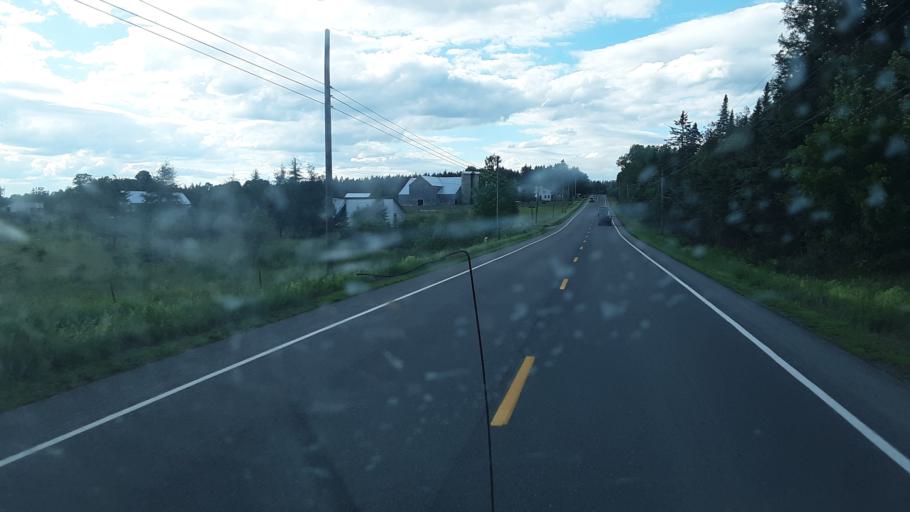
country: US
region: Maine
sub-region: Penobscot County
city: Patten
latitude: 45.9347
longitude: -68.4491
